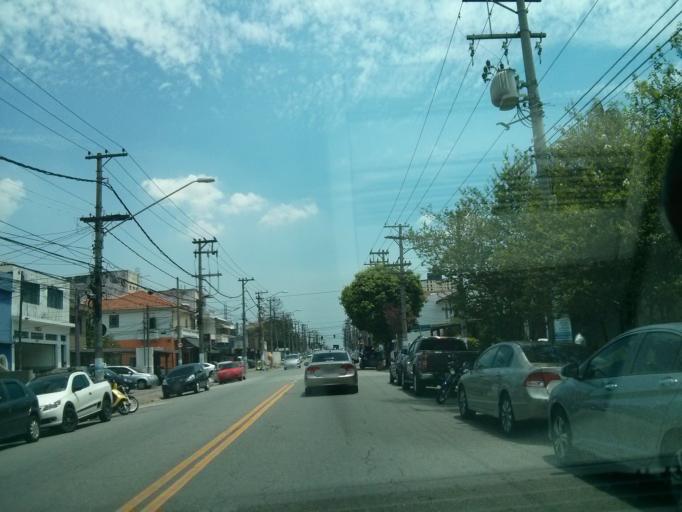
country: BR
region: Sao Paulo
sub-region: Sao Paulo
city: Sao Paulo
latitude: -23.6065
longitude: -46.6164
